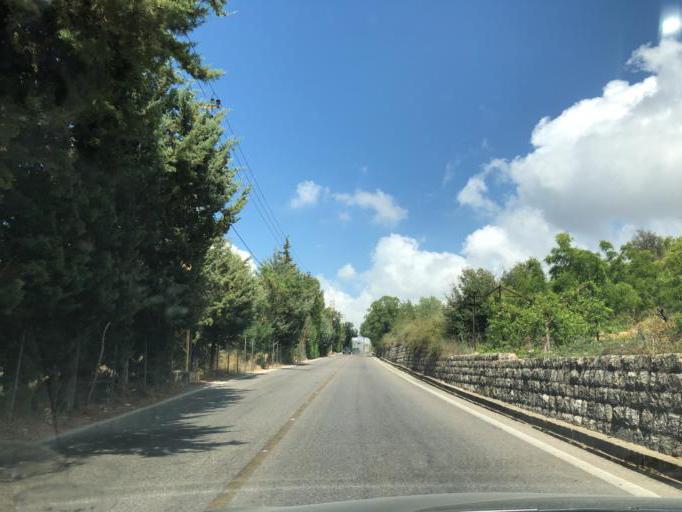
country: LB
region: Mont-Liban
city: Beit ed Dine
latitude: 33.6973
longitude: 35.5890
